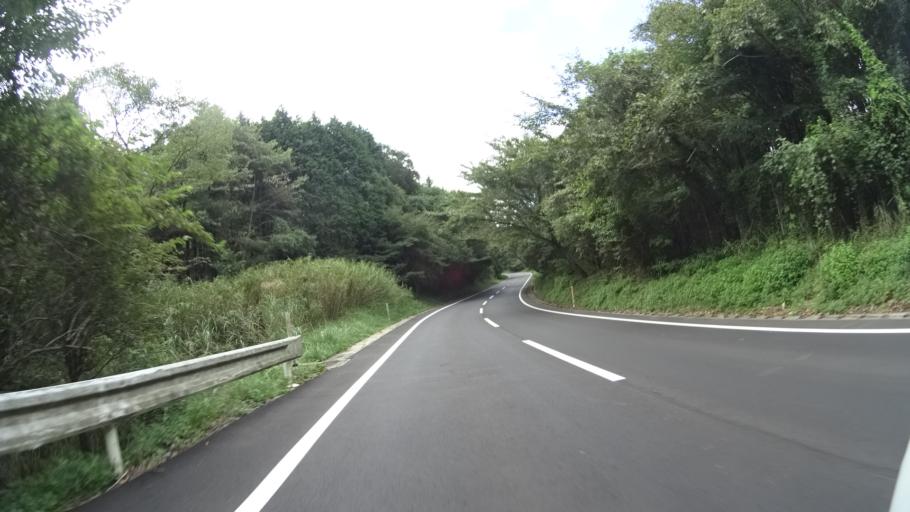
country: JP
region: Oita
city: Beppu
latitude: 33.3277
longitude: 131.4185
